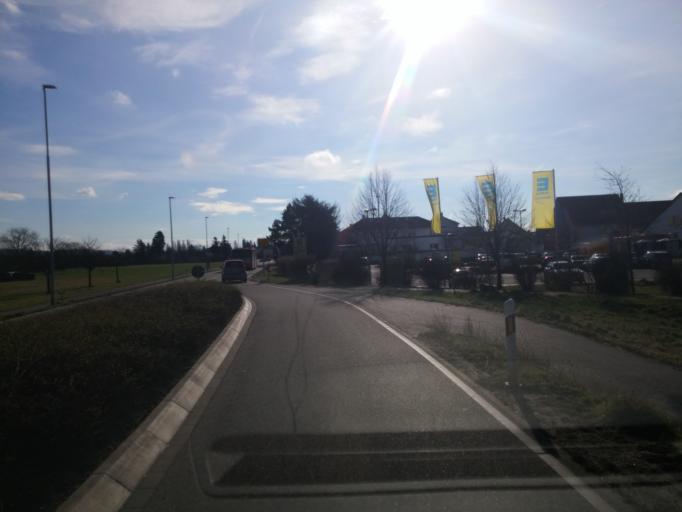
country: DE
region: Baden-Wuerttemberg
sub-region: Karlsruhe Region
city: Karlsdorf-Neuthard
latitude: 49.1192
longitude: 8.5147
